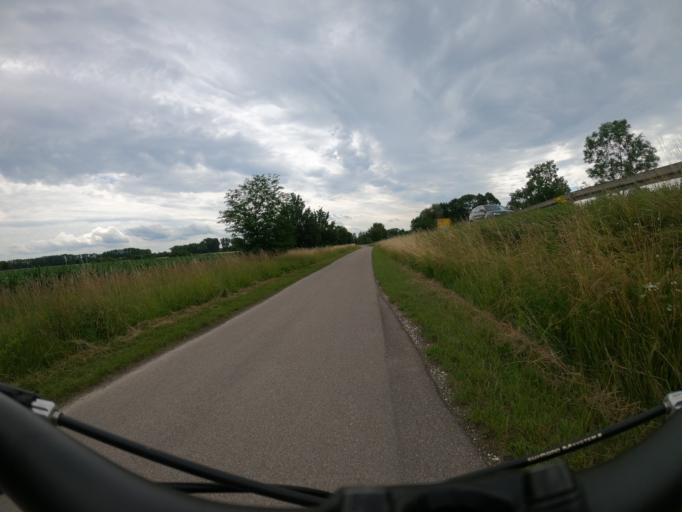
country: DE
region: Bavaria
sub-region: Swabia
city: Nersingen
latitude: 48.4326
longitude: 10.0625
